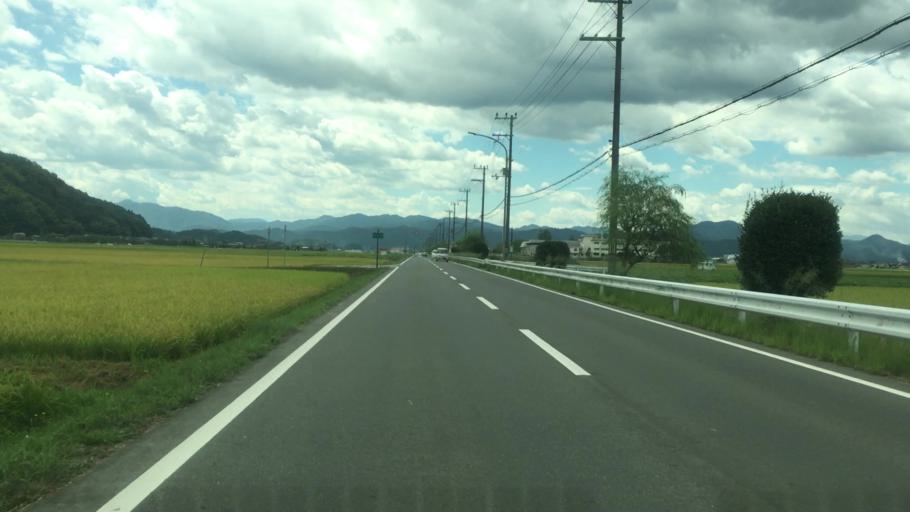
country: JP
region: Hyogo
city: Toyooka
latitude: 35.5357
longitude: 134.8397
